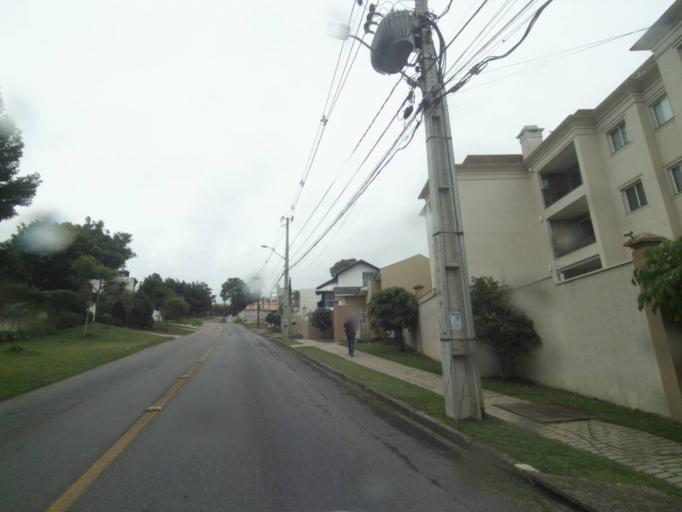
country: BR
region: Parana
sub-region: Curitiba
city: Curitiba
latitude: -25.4241
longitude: -49.3250
